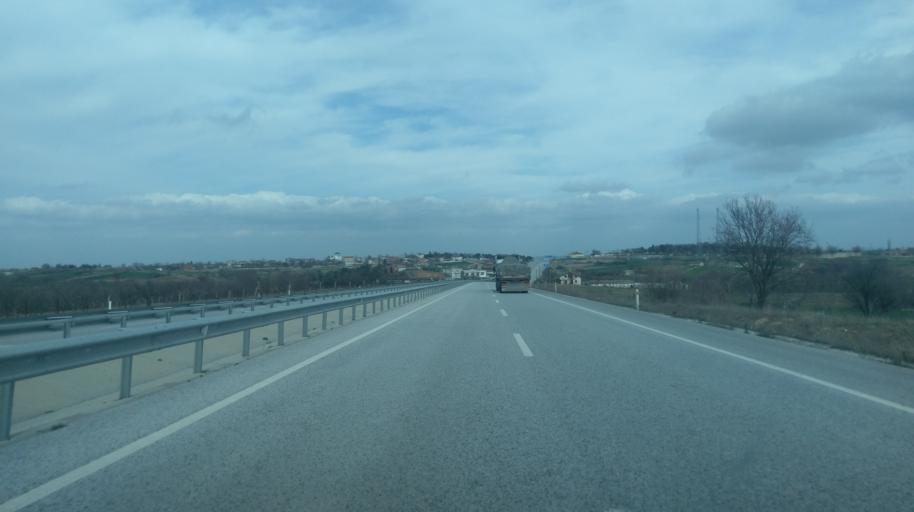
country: TR
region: Edirne
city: Kircasalih
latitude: 41.3831
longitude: 26.7916
